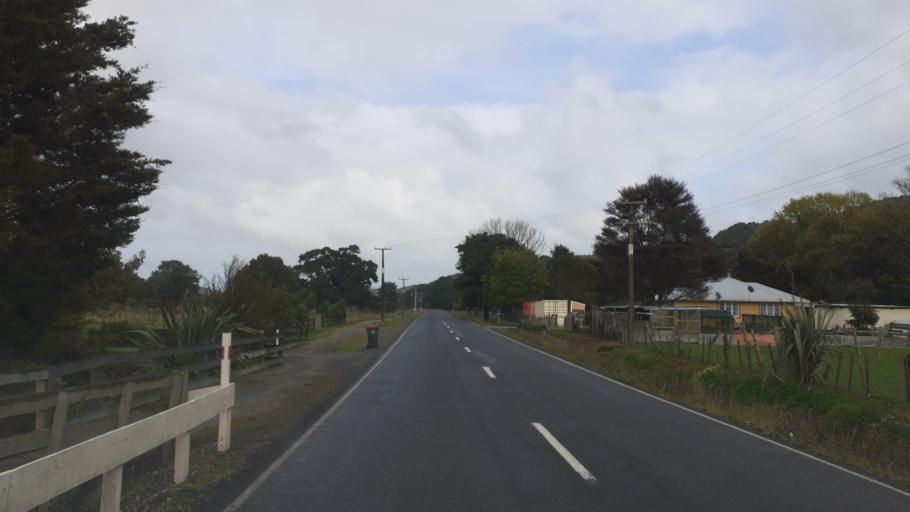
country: NZ
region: Northland
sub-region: Far North District
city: Moerewa
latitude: -35.3984
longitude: 173.9993
